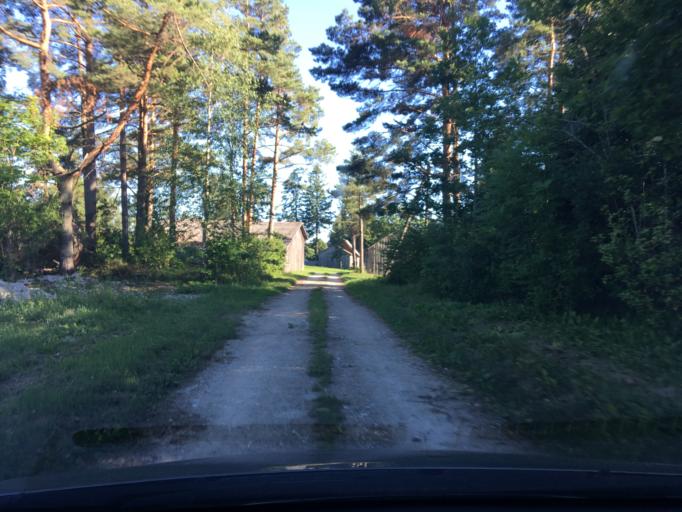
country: EE
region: Laeaene
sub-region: Lihula vald
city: Lihula
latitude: 58.5841
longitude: 23.7361
